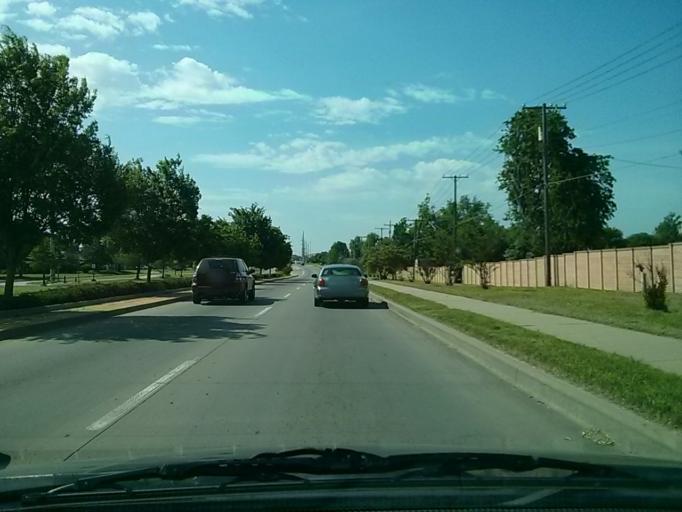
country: US
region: Oklahoma
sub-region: Tulsa County
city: Tulsa
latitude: 36.1833
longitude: -95.9760
